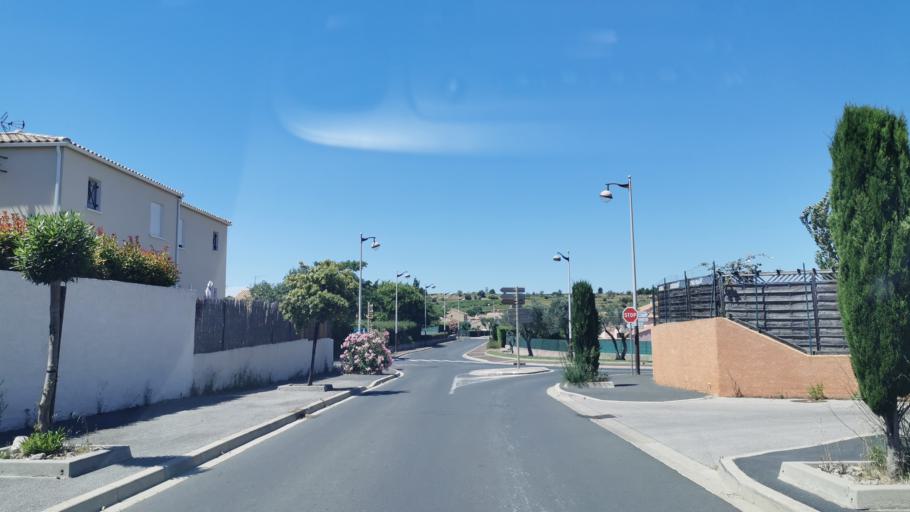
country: FR
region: Languedoc-Roussillon
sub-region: Departement de l'Aude
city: Fleury
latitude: 43.2308
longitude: 3.1411
